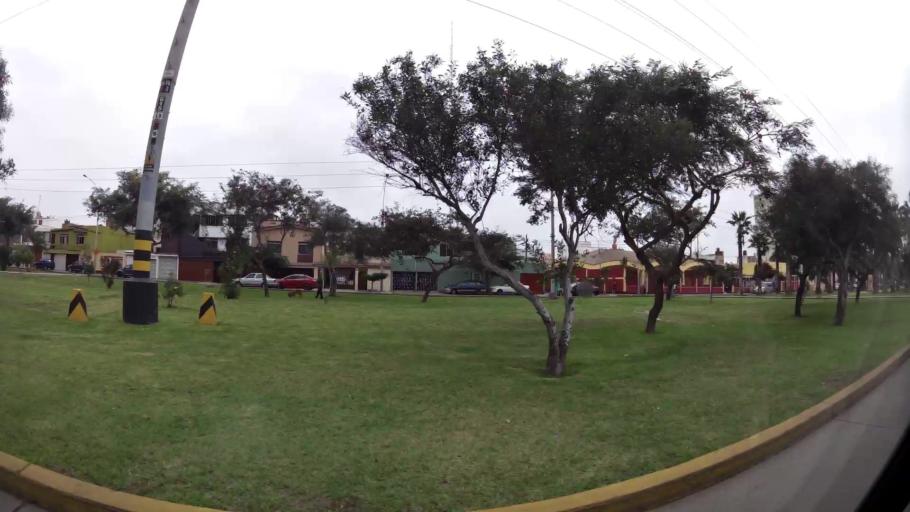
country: PE
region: Callao
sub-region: Callao
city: Callao
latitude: -12.0699
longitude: -77.0929
